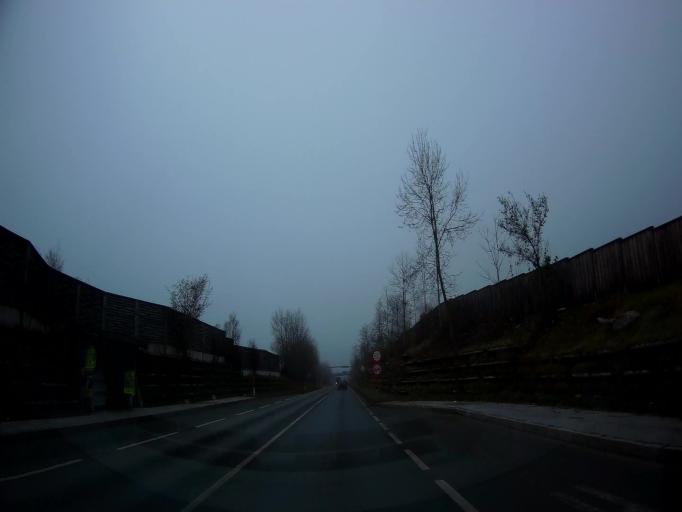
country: AT
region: Salzburg
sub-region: Politischer Bezirk Zell am See
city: Maishofen
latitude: 47.3490
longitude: 12.7999
